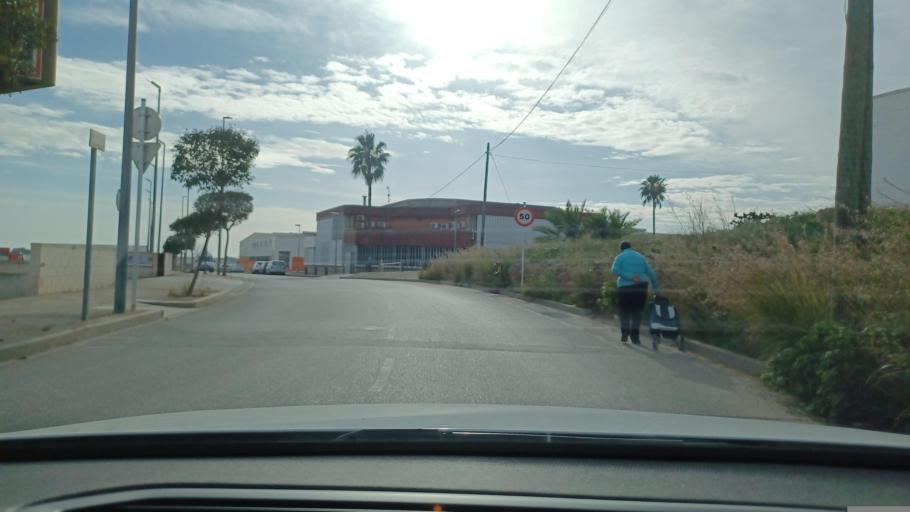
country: ES
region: Catalonia
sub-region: Provincia de Tarragona
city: Amposta
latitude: 40.7011
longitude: 0.5748
